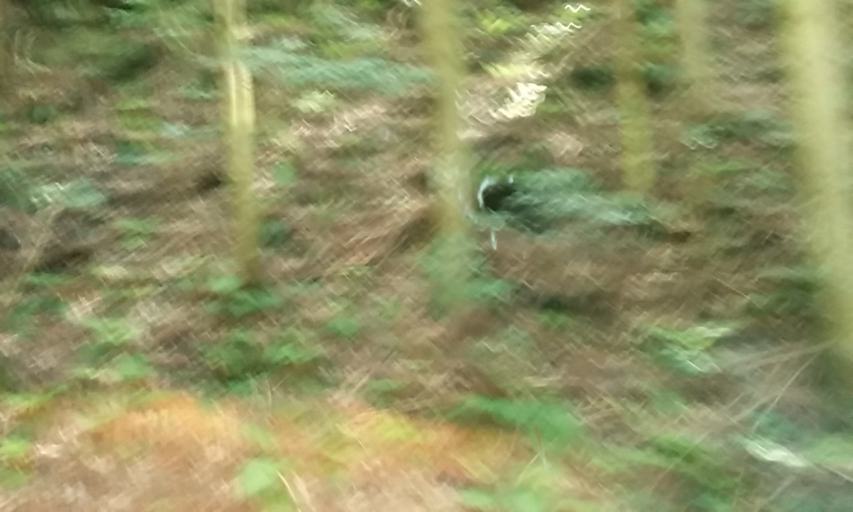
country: JP
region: Ehime
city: Niihama
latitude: 33.8680
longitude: 133.2953
